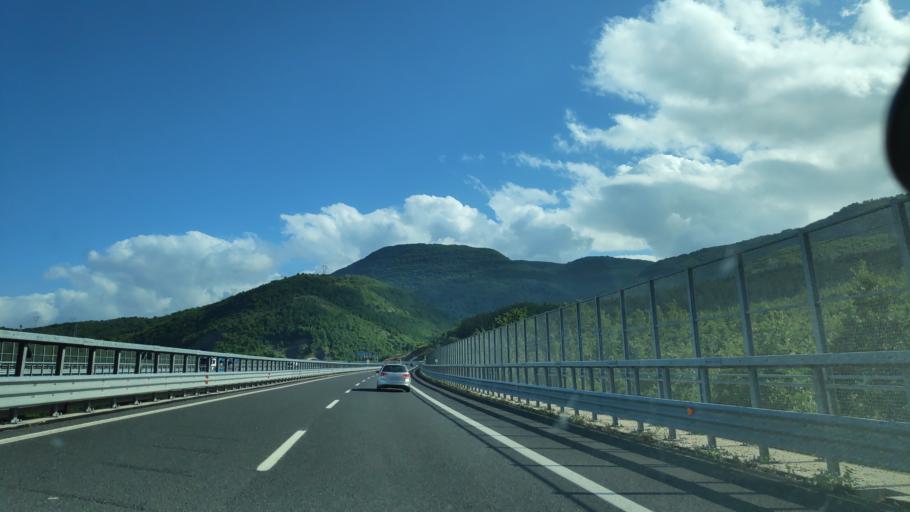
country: IT
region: Campania
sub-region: Provincia di Salerno
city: Casalbuono
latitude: 40.2223
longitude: 15.6718
